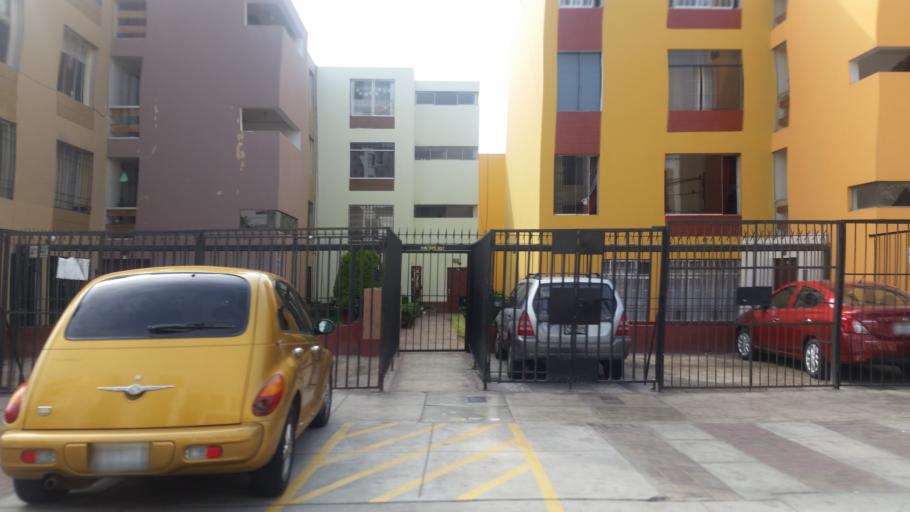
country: PE
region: Lima
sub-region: Lima
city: San Isidro
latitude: -12.0956
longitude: -77.0730
